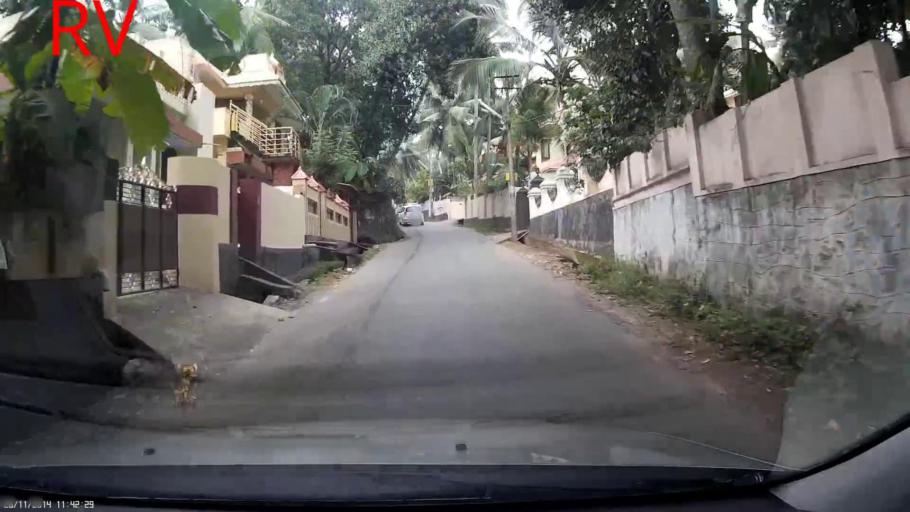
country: IN
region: Kerala
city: Kovalam
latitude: 8.4024
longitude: 77.0135
